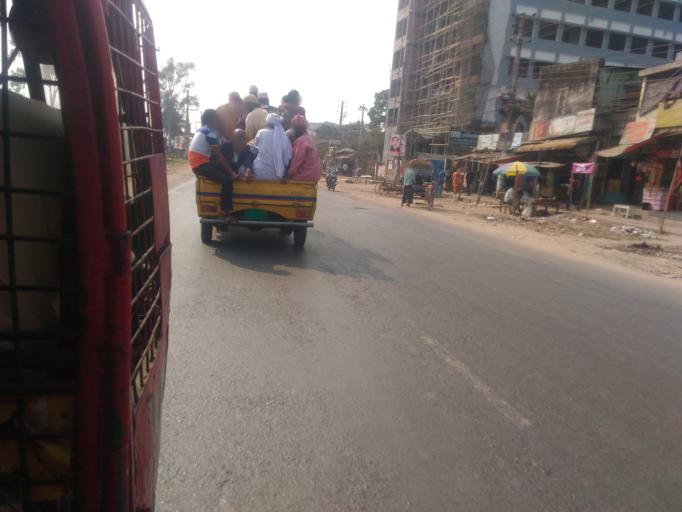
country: BD
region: Dhaka
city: Tungi
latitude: 23.9937
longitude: 90.4074
